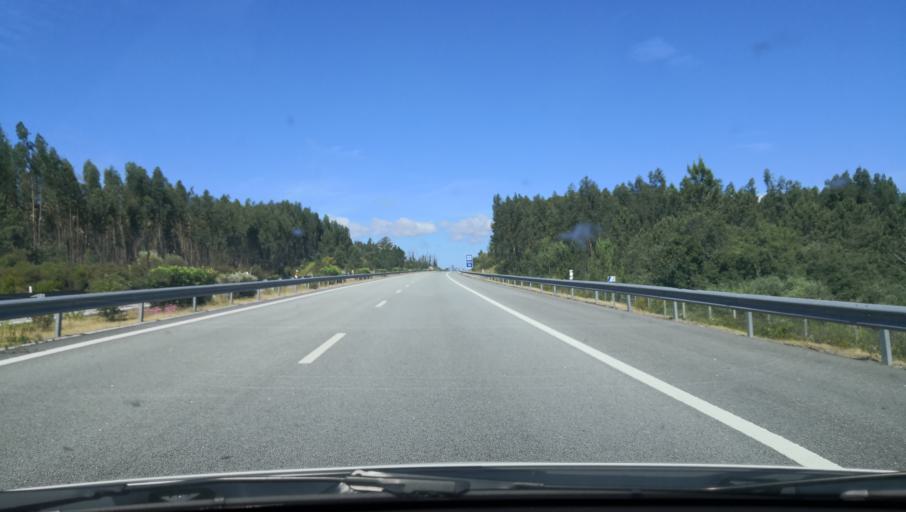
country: PT
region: Coimbra
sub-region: Cantanhede
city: Cantanhede
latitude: 40.2840
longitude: -8.5424
